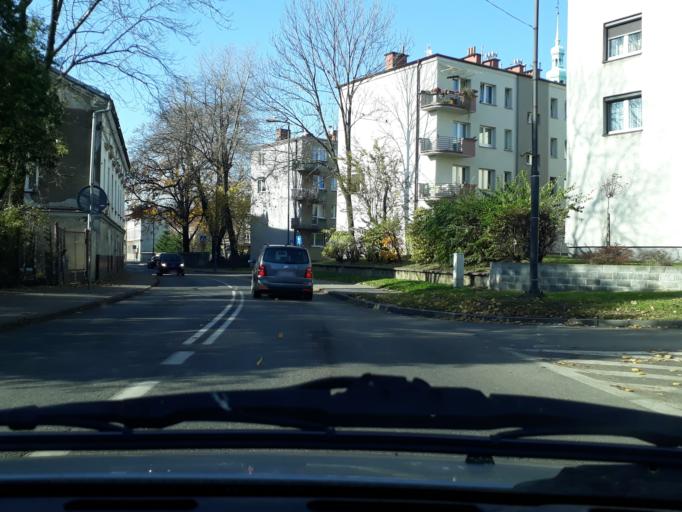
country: PL
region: Silesian Voivodeship
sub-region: Powiat tarnogorski
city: Tarnowskie Gory
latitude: 50.4420
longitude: 18.8548
